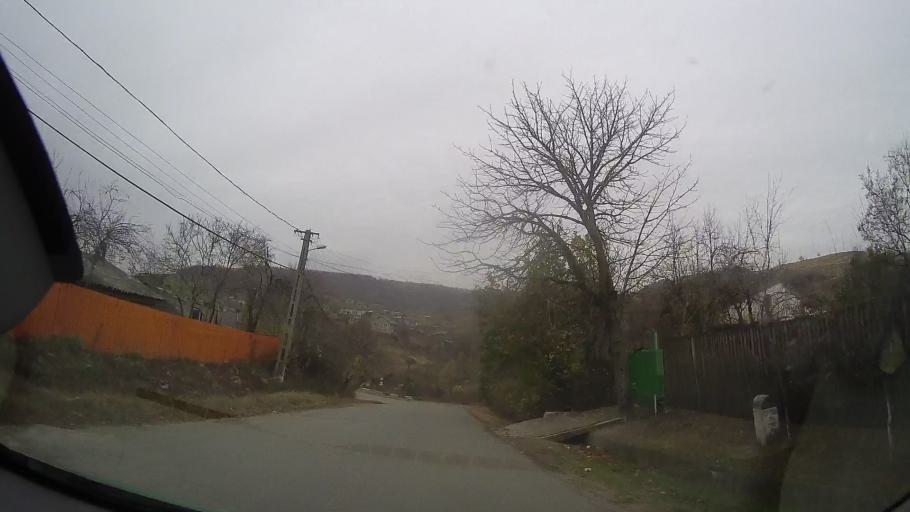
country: RO
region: Prahova
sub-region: Comuna Gornet-Cricov
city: Gornet-Cricov
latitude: 45.0545
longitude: 26.2938
